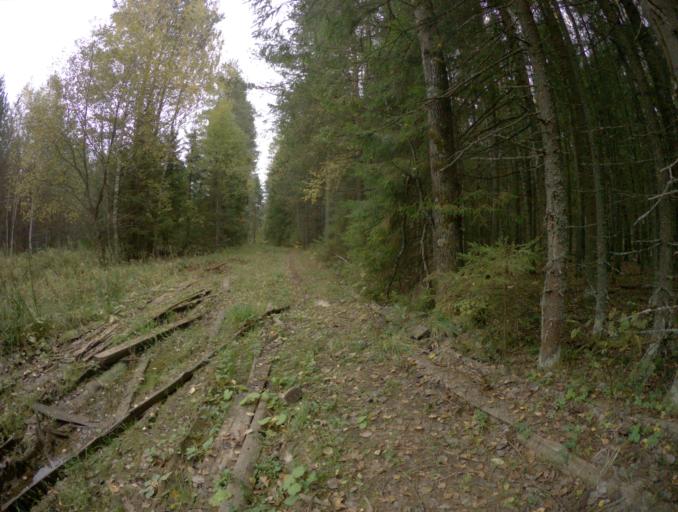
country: RU
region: Vladimir
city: Stepantsevo
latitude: 56.3137
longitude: 41.5894
